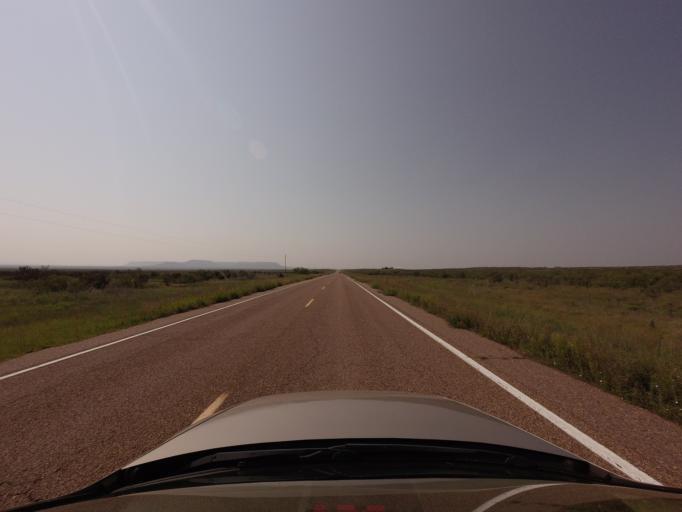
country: US
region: New Mexico
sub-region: Quay County
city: Tucumcari
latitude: 35.0828
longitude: -103.7376
